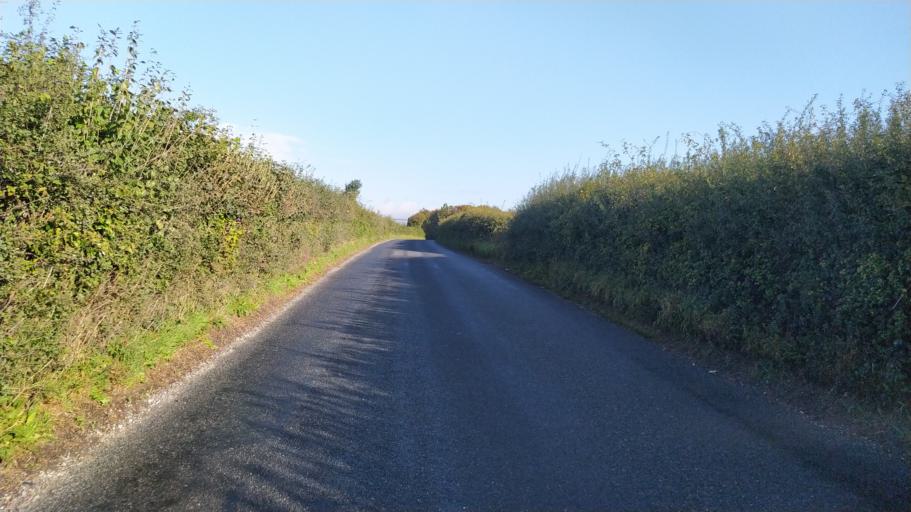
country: GB
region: England
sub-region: Wiltshire
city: Ansty
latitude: 50.9215
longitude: -2.0542
